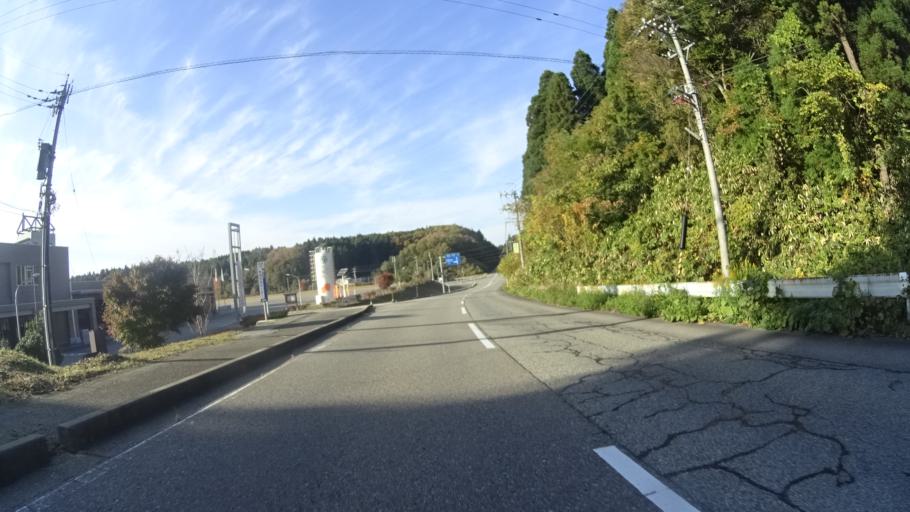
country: JP
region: Ishikawa
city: Hakui
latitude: 37.0071
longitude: 136.8004
